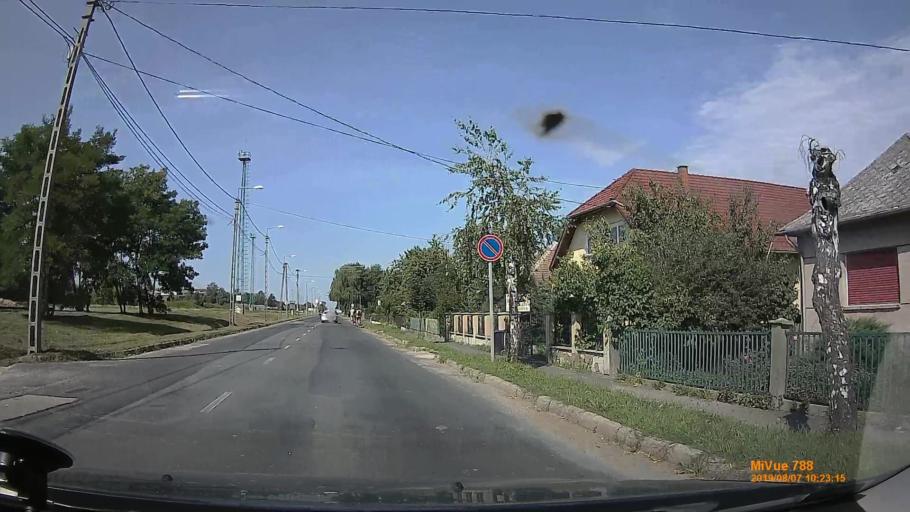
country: HU
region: Zala
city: Lenti
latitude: 46.6223
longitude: 16.5283
